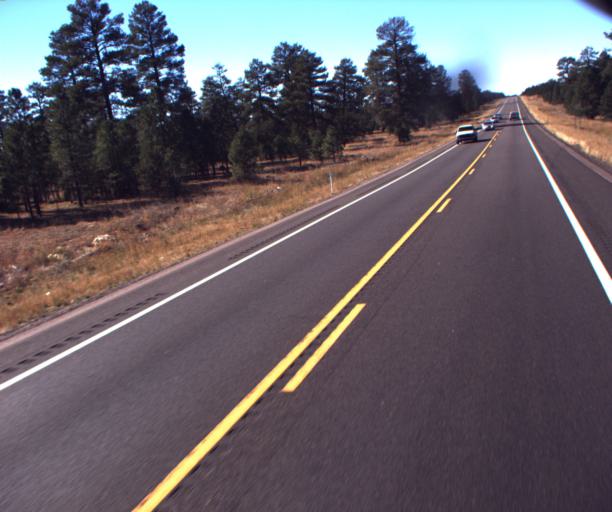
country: US
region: Arizona
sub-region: Apache County
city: Saint Michaels
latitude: 35.7012
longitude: -109.2935
